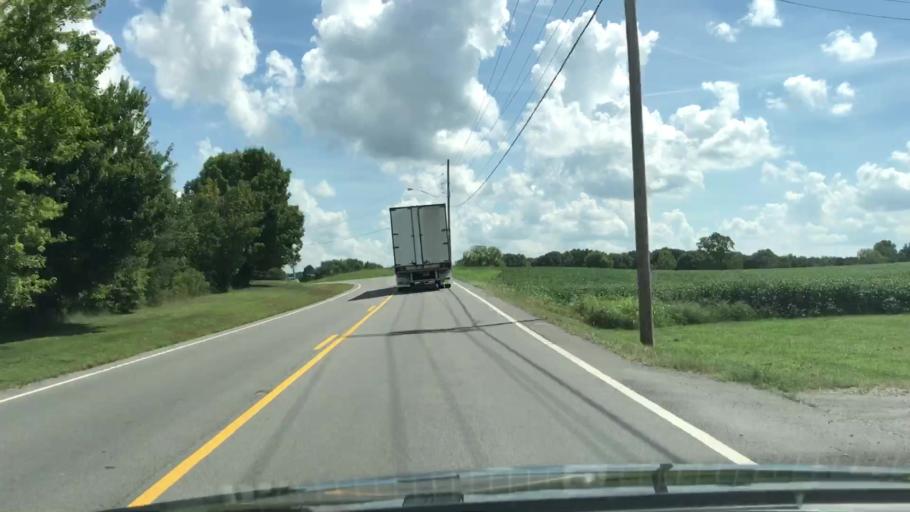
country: US
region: Tennessee
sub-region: Robertson County
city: Cross Plains
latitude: 36.5390
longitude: -86.6654
